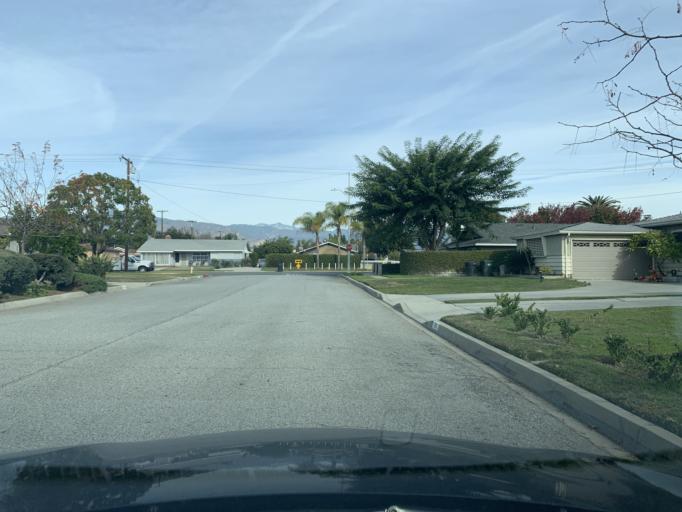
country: US
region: California
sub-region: Los Angeles County
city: West Covina
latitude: 34.0785
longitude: -117.9297
